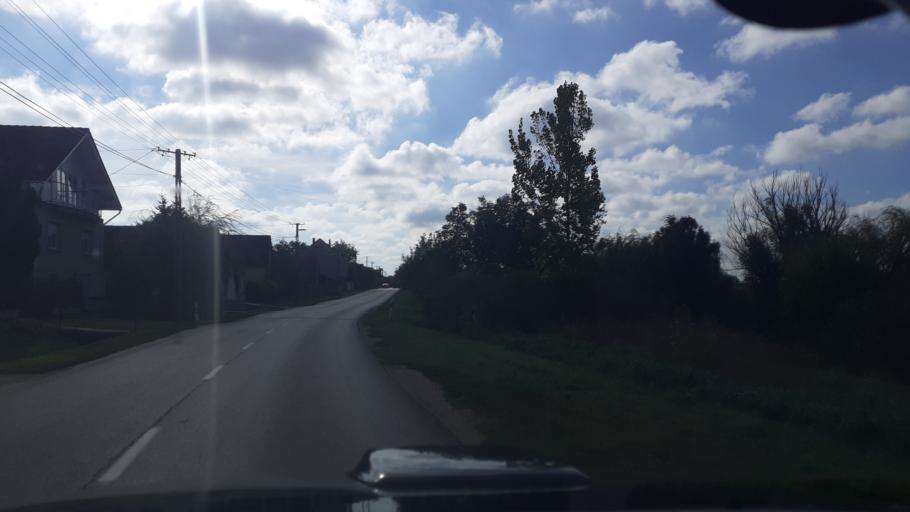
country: HU
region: Fejer
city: Baracs
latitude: 46.9169
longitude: 18.8818
